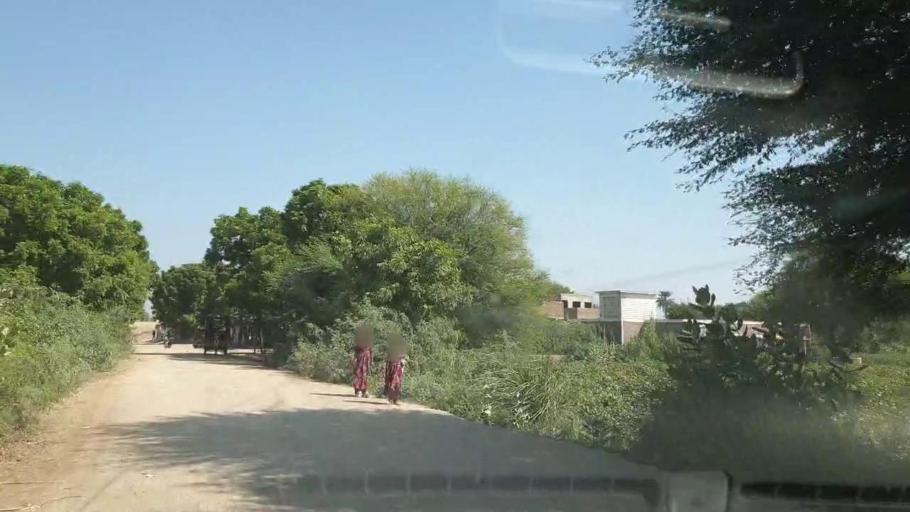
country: PK
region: Sindh
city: Tando Jam
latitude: 25.3997
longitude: 68.5861
